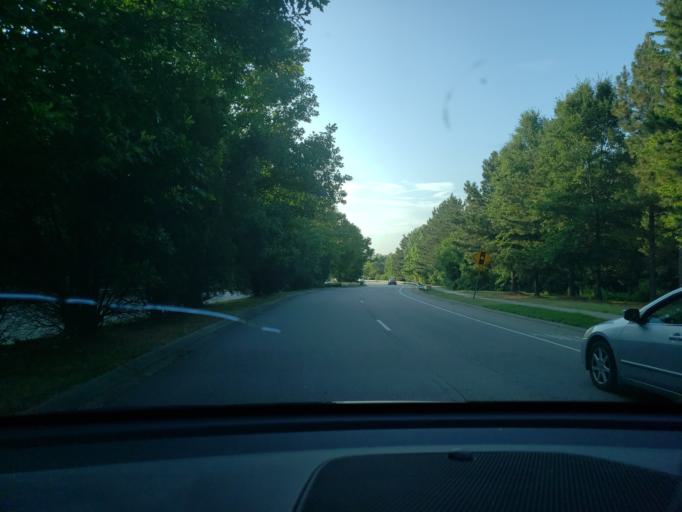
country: US
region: North Carolina
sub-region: Durham County
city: Durham
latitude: 35.9440
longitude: -78.9206
